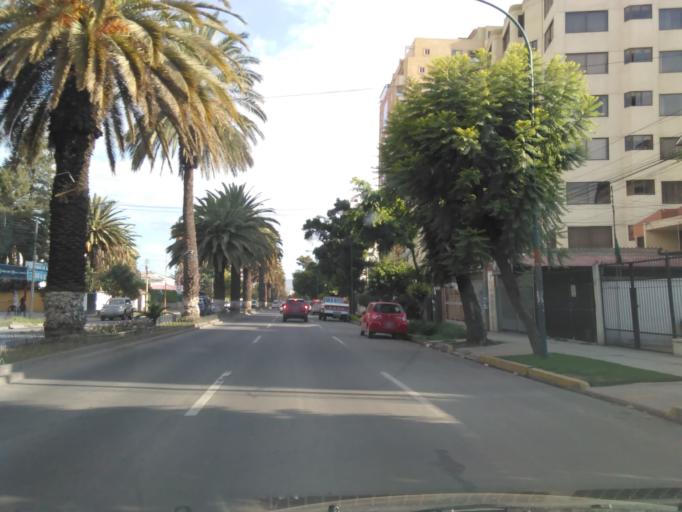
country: BO
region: Cochabamba
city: Cochabamba
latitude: -17.3696
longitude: -66.1636
